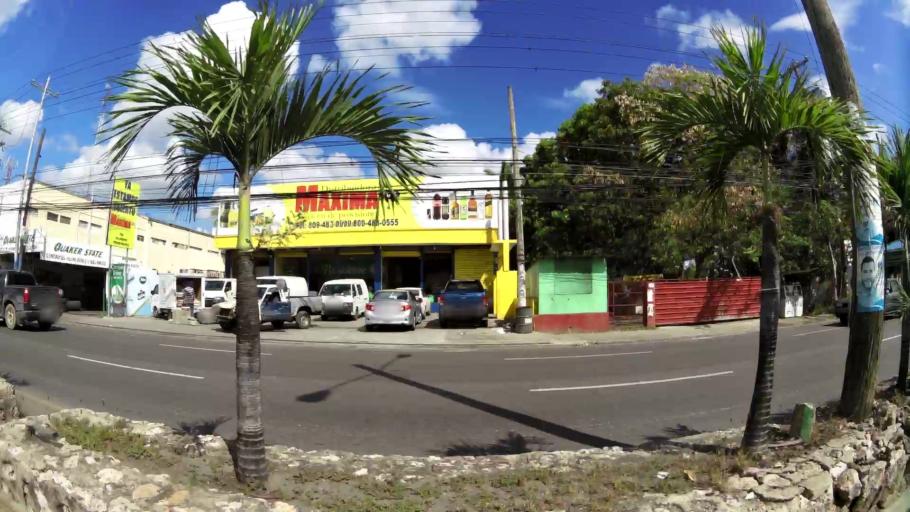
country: DO
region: Santo Domingo
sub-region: Santo Domingo
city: Santo Domingo Este
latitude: 18.5157
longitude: -69.8411
